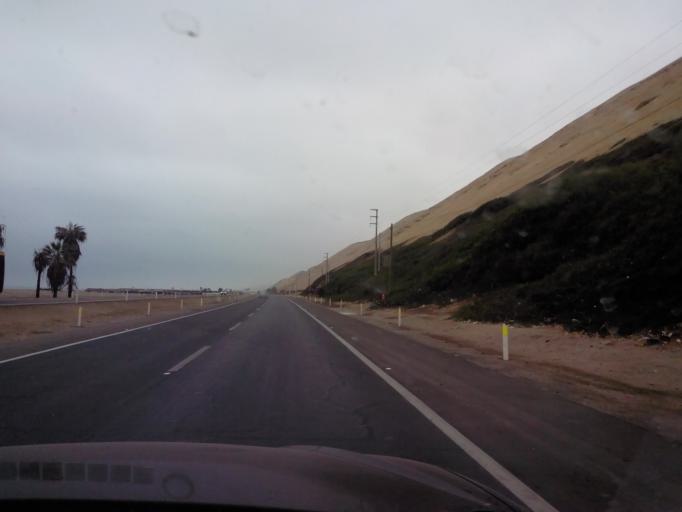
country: PE
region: Ica
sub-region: Provincia de Chincha
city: San Pedro
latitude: -13.3461
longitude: -76.2264
